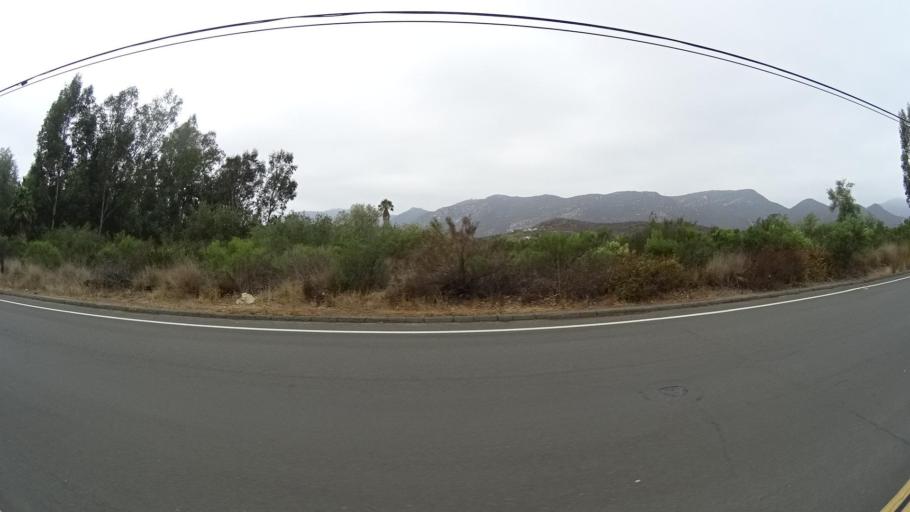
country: US
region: California
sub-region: San Diego County
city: Escondido
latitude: 33.0821
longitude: -117.1049
